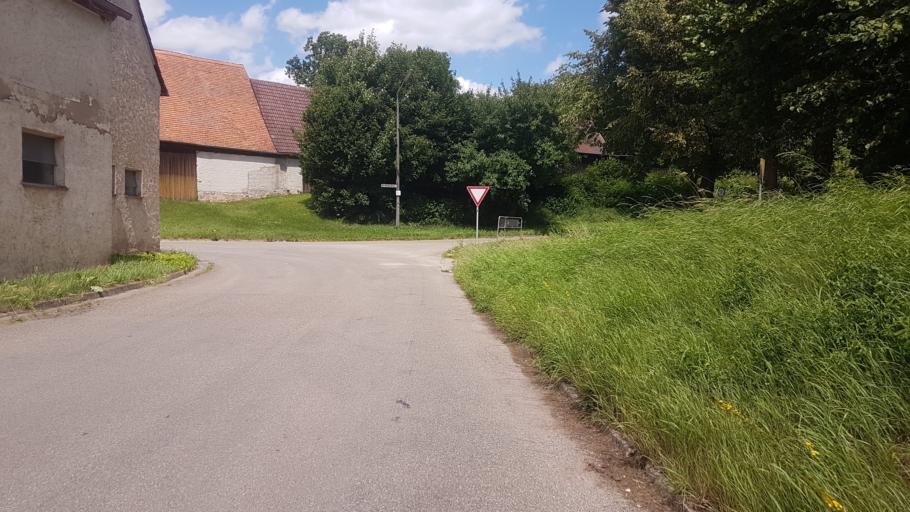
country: DE
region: Bavaria
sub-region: Regierungsbezirk Mittelfranken
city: Colmberg
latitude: 49.3365
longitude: 10.3764
